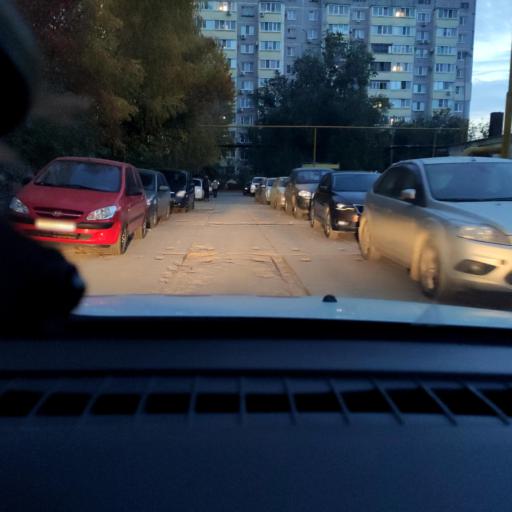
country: RU
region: Samara
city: Samara
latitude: 53.1062
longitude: 50.0823
